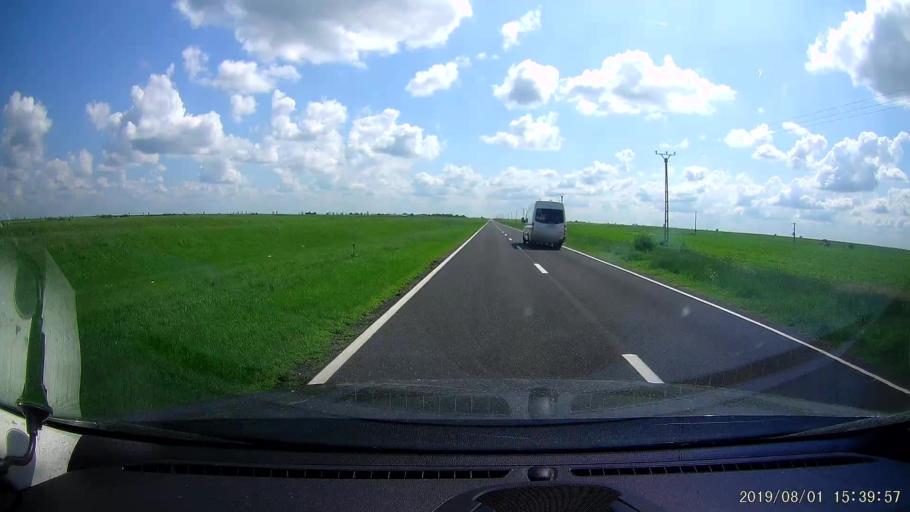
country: RO
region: Braila
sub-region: Comuna Baraganul
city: Baraganul
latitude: 44.8465
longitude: 27.5503
